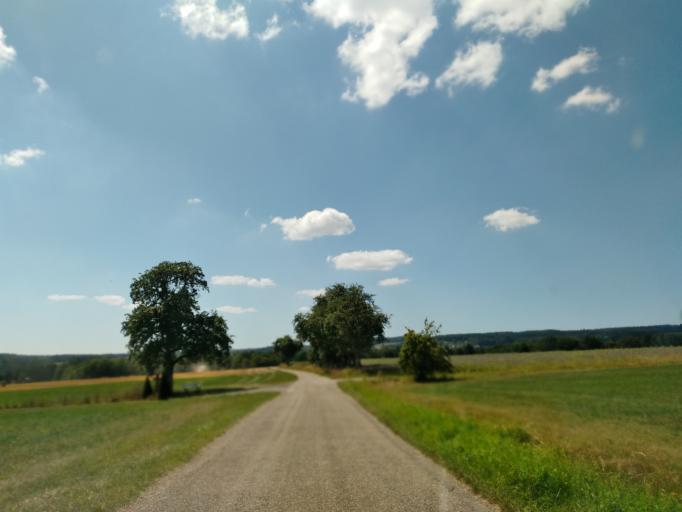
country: DE
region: Baden-Wuerttemberg
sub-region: Karlsruhe Region
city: Limbach
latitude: 49.4553
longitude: 9.2358
